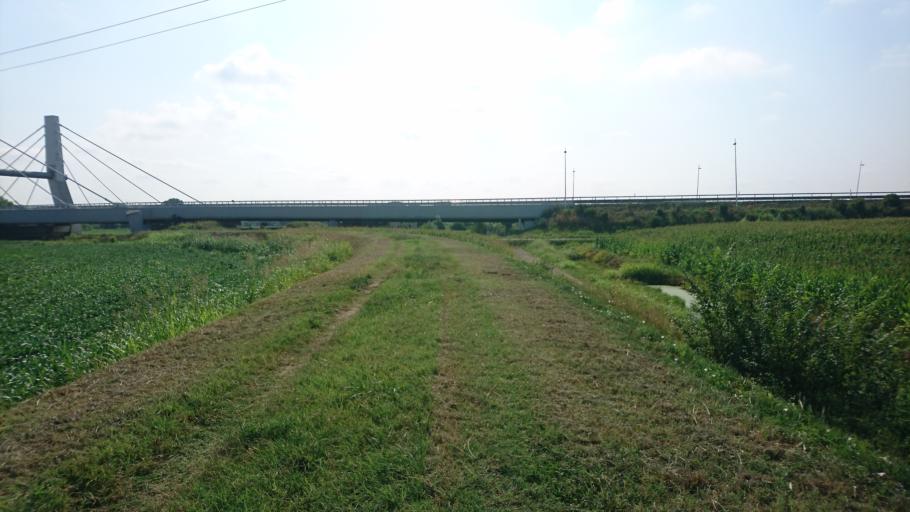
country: IT
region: Veneto
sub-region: Provincia di Vicenza
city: Villaganzerla
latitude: 45.4606
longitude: 11.6292
